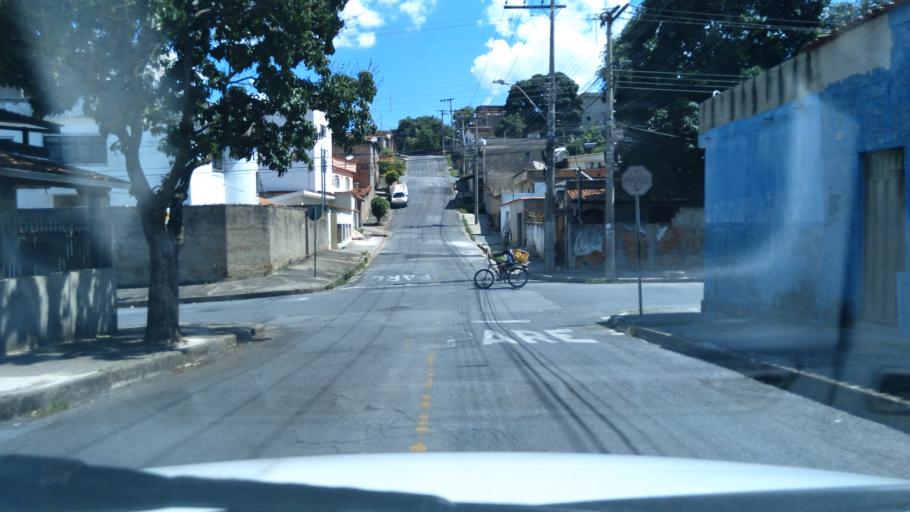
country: BR
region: Minas Gerais
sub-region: Belo Horizonte
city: Belo Horizonte
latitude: -19.8661
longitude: -43.9164
